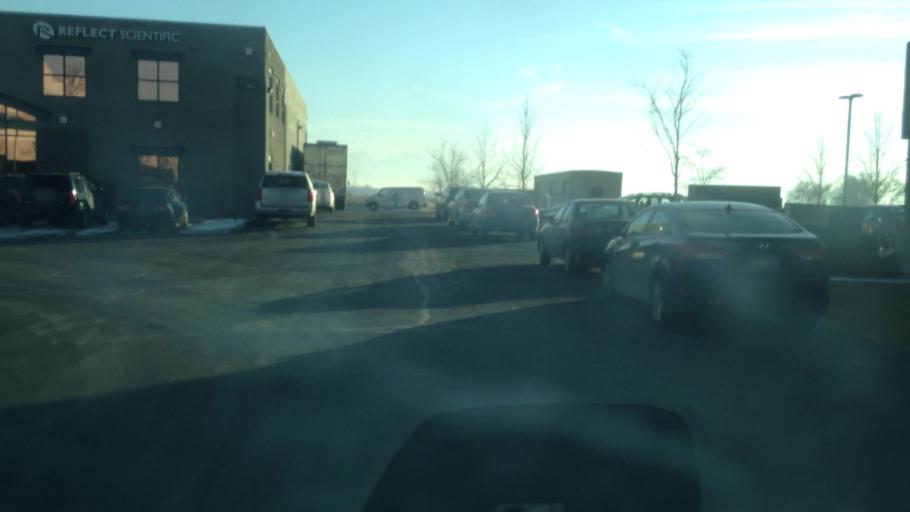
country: US
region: Utah
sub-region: Utah County
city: Orem
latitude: 40.2740
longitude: -111.7285
